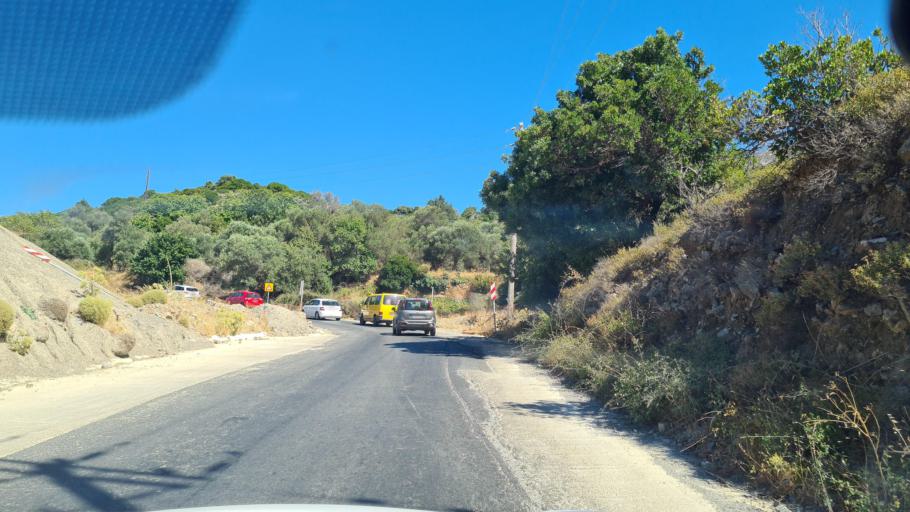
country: GR
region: Crete
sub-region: Nomos Chanias
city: Vryses
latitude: 35.3619
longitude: 23.6247
